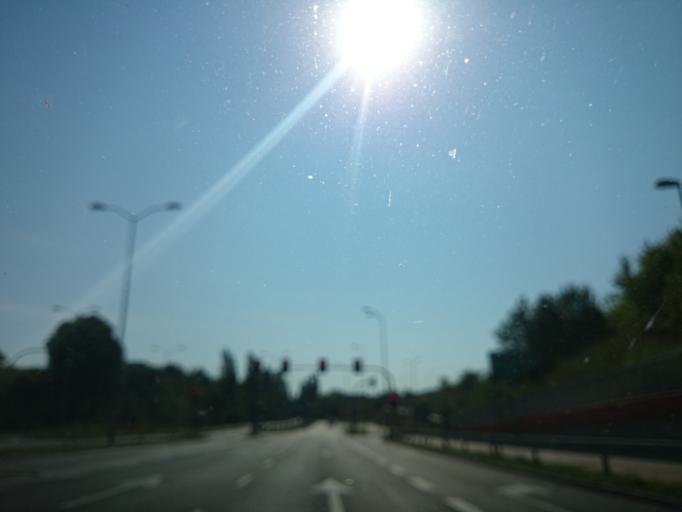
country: PL
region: West Pomeranian Voivodeship
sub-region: Powiat policki
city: Przeclaw
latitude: 53.3881
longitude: 14.5133
